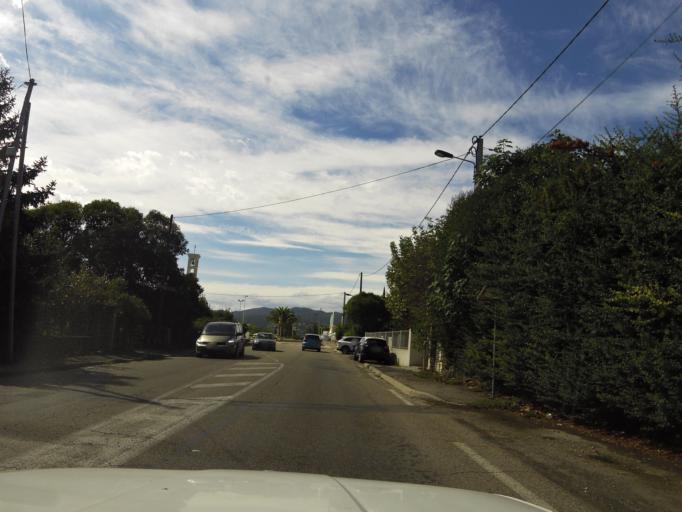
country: FR
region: Languedoc-Roussillon
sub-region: Departement du Gard
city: Ales
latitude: 44.1140
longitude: 4.1045
